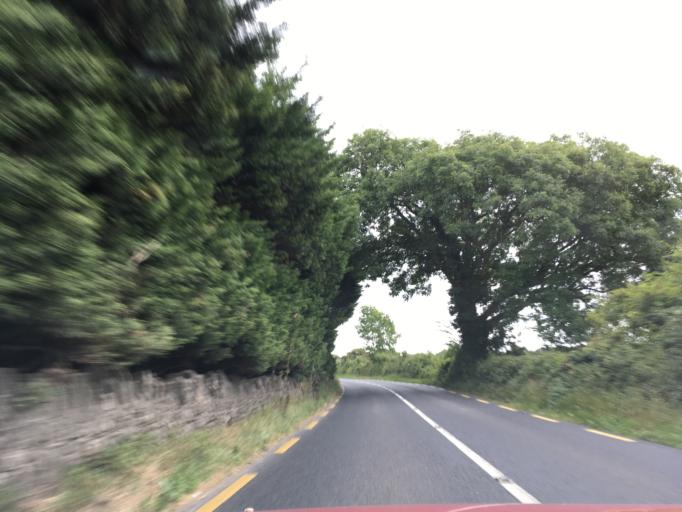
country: IE
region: Munster
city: Cashel
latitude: 52.4440
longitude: -7.8028
